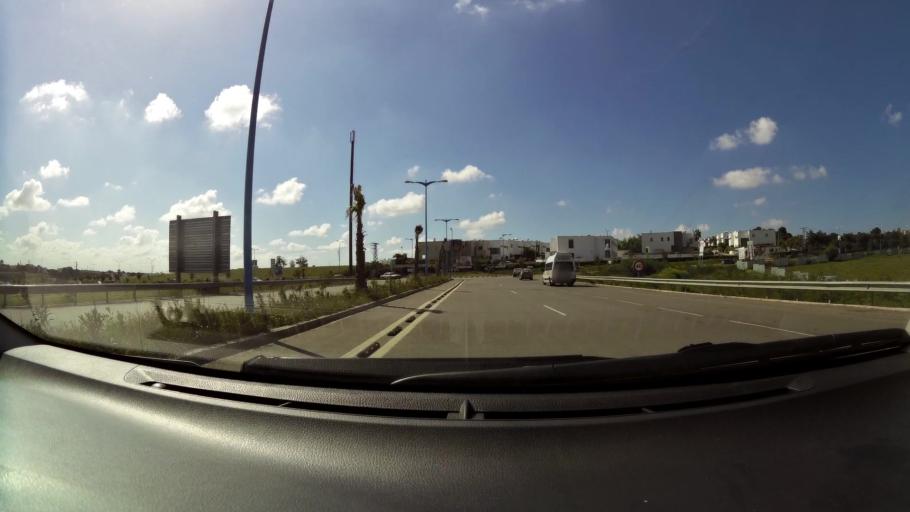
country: MA
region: Grand Casablanca
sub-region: Nouaceur
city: Bouskoura
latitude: 33.4842
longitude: -7.6348
